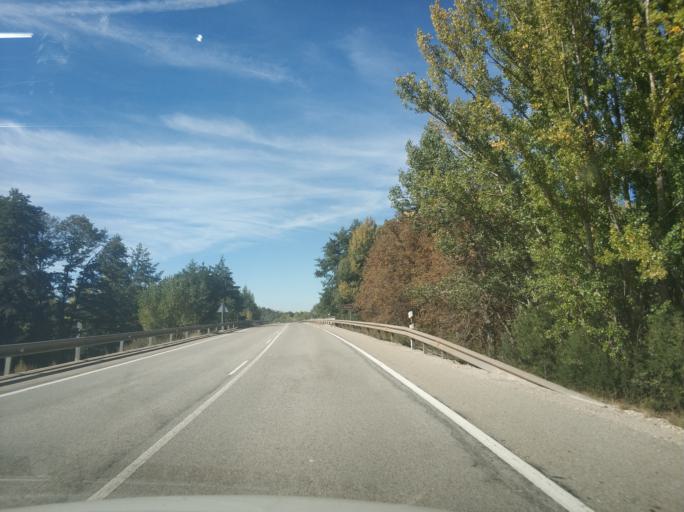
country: ES
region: Castille and Leon
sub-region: Provincia de Burgos
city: Barbadillo del Mercado
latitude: 42.0471
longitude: -3.3630
